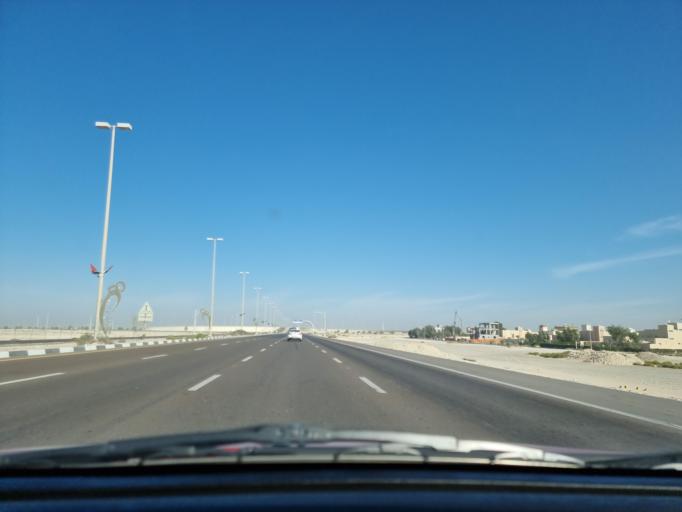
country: AE
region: Abu Dhabi
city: Abu Dhabi
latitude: 24.4053
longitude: 54.7164
